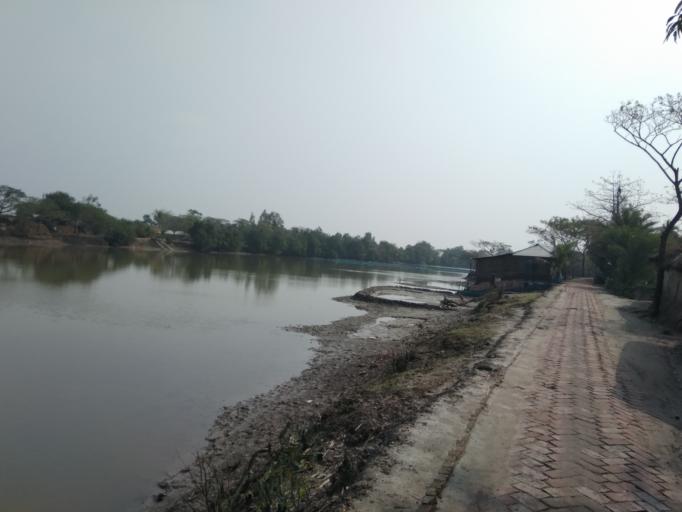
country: IN
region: West Bengal
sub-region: North 24 Parganas
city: Gosaba
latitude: 22.2378
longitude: 89.1446
